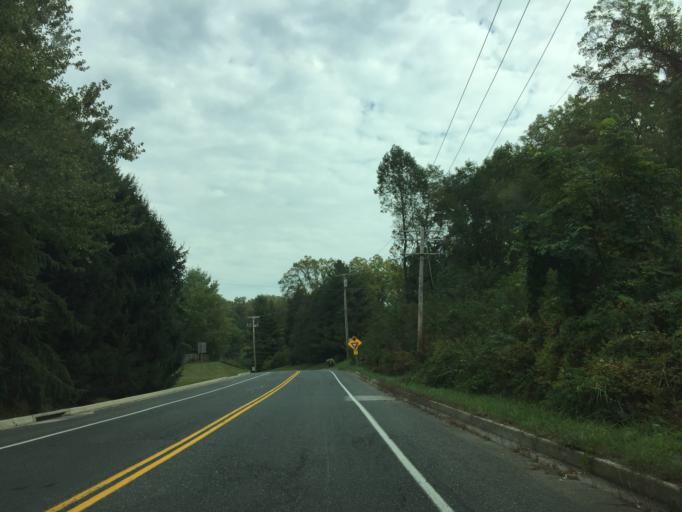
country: US
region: Maryland
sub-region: Harford County
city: Bel Air South
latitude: 39.4936
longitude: -76.3183
